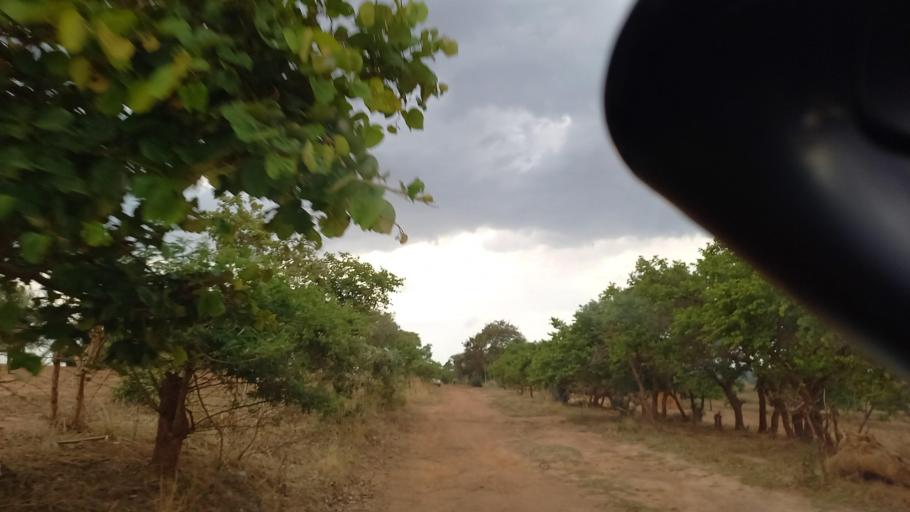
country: ZM
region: Lusaka
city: Kafue
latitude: -16.1327
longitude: 28.0575
